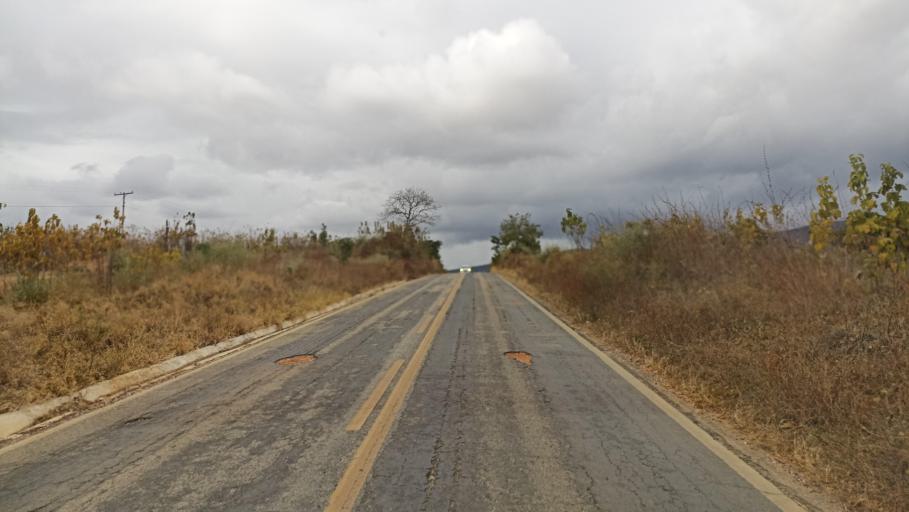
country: BR
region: Minas Gerais
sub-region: Itinga
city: Itinga
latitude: -16.6267
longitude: -41.7851
